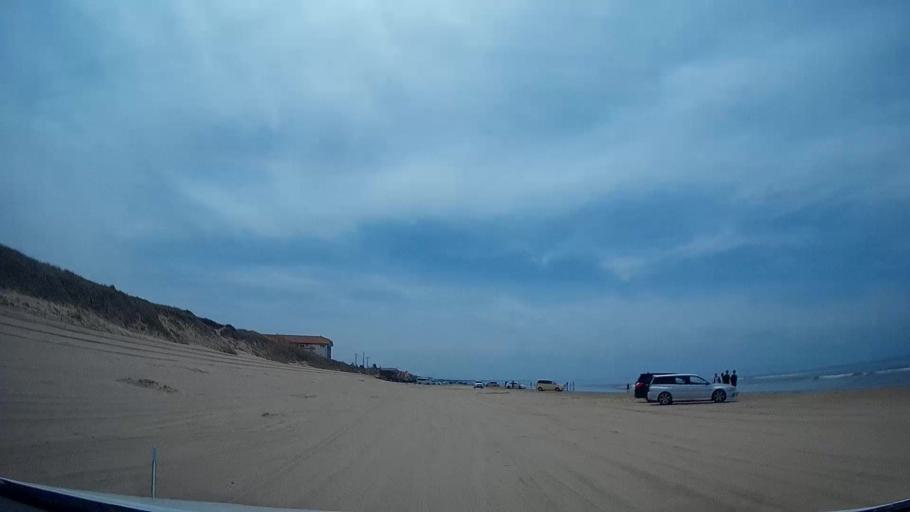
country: JP
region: Ishikawa
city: Hakui
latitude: 36.8951
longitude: 136.7663
